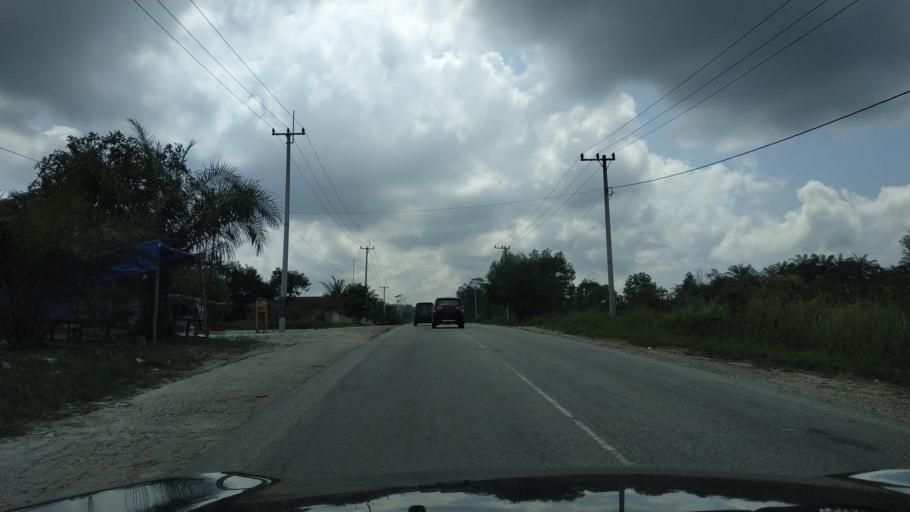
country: ID
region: Riau
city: Pangkalanbunut
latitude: 0.3027
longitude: 101.9139
